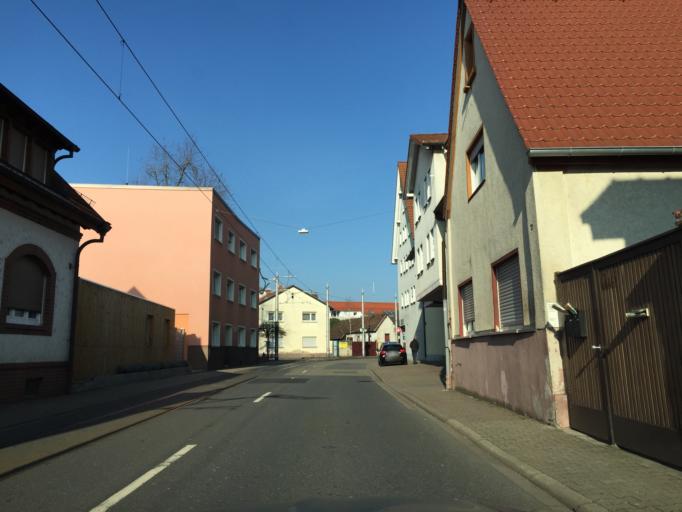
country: DE
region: Baden-Wuerttemberg
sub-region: Karlsruhe Region
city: Eppelheim
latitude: 49.4009
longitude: 8.6276
